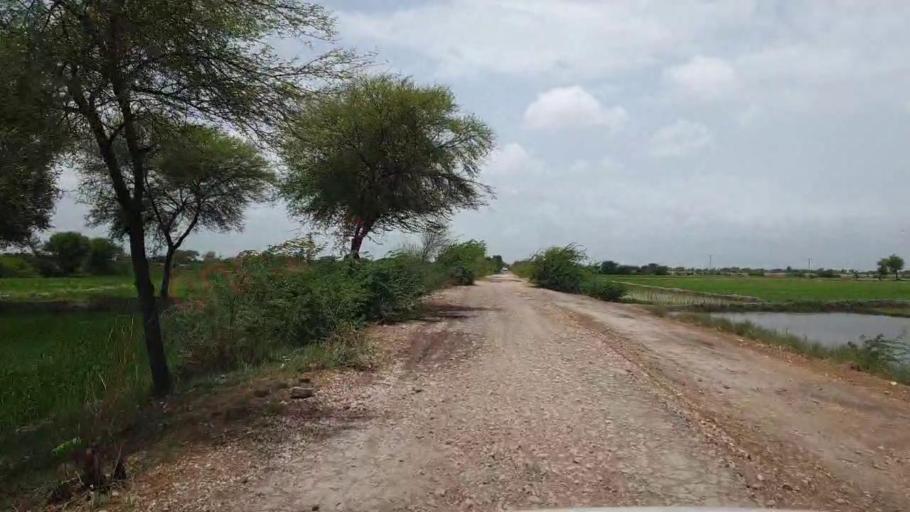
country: PK
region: Sindh
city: Kario
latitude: 24.7233
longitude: 68.5641
